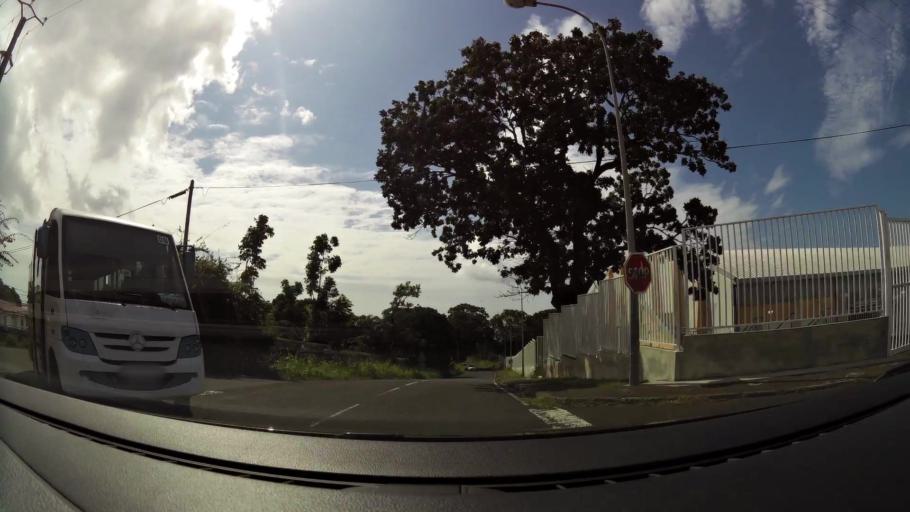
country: GP
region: Guadeloupe
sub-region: Guadeloupe
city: Saint-Claude
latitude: 16.0170
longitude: -61.7162
